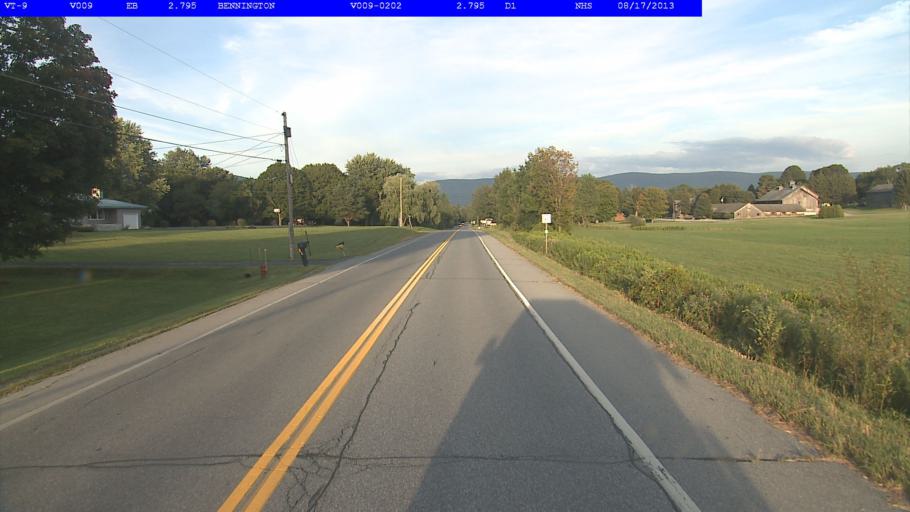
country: US
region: Vermont
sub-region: Bennington County
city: Bennington
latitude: 42.8821
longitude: -73.2245
